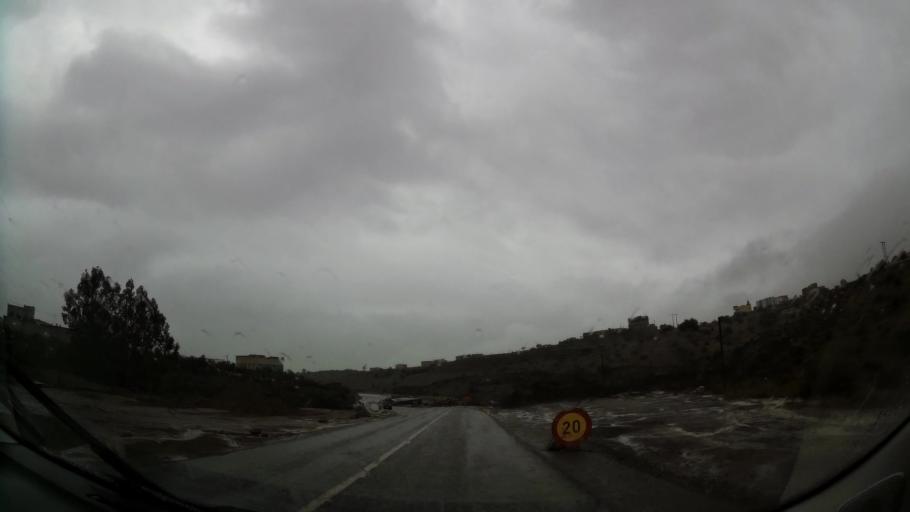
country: MA
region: Oriental
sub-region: Nador
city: Midar
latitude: 34.8905
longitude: -3.7407
